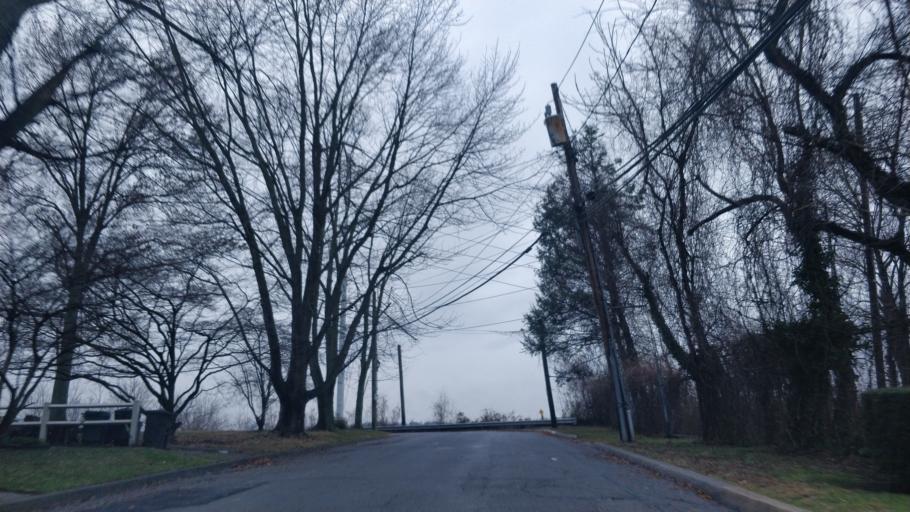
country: US
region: New York
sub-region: Nassau County
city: Glenwood Landing
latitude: 40.8274
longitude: -73.6458
